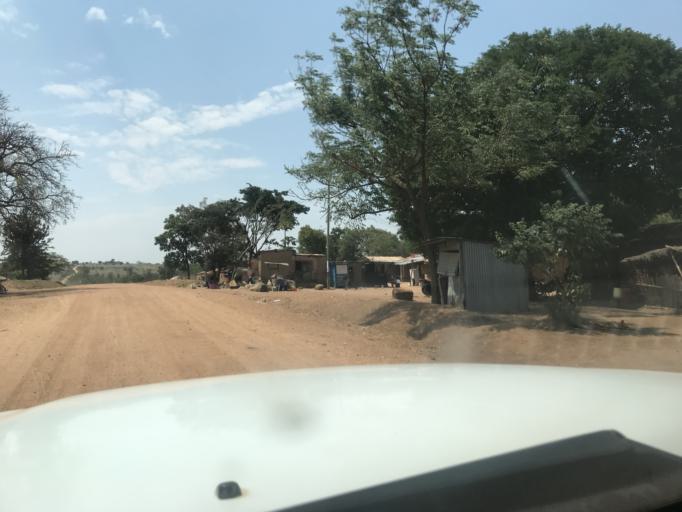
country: TZ
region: Mara
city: Nyamuswa
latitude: -1.9424
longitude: 33.9982
